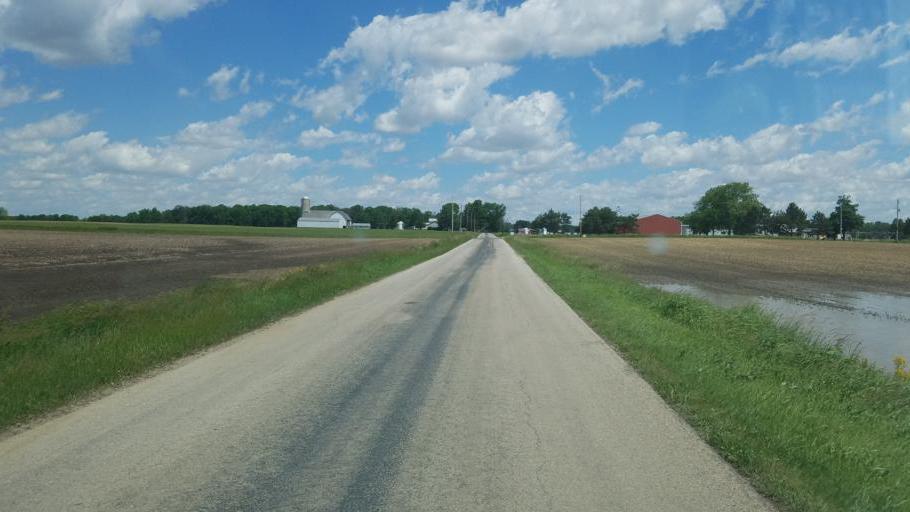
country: US
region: Ohio
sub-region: Richland County
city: Shelby
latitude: 40.9285
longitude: -82.7050
